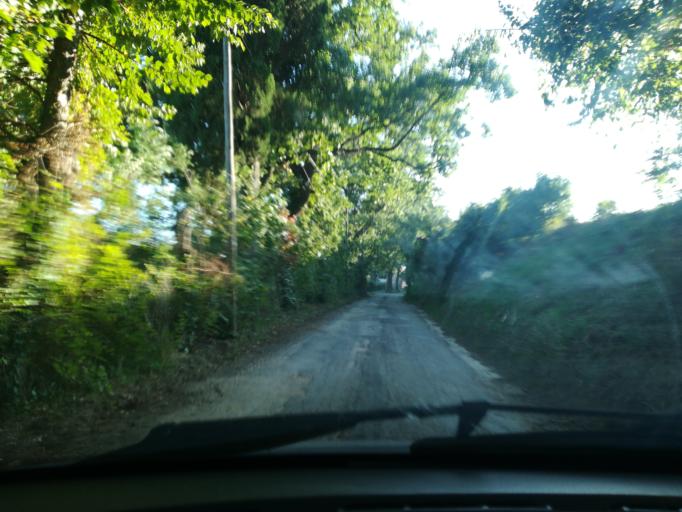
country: IT
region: The Marches
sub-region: Provincia di Macerata
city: Macerata
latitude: 43.2797
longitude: 13.4518
